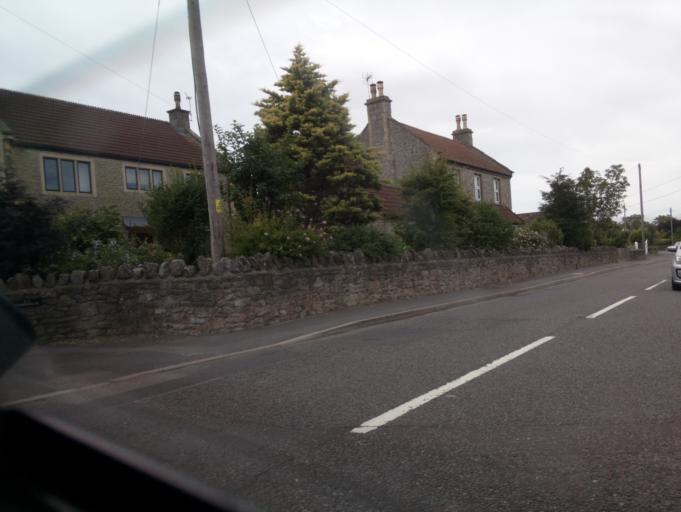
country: GB
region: England
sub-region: North Somerset
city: Congresbury
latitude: 51.3670
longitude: -2.8069
